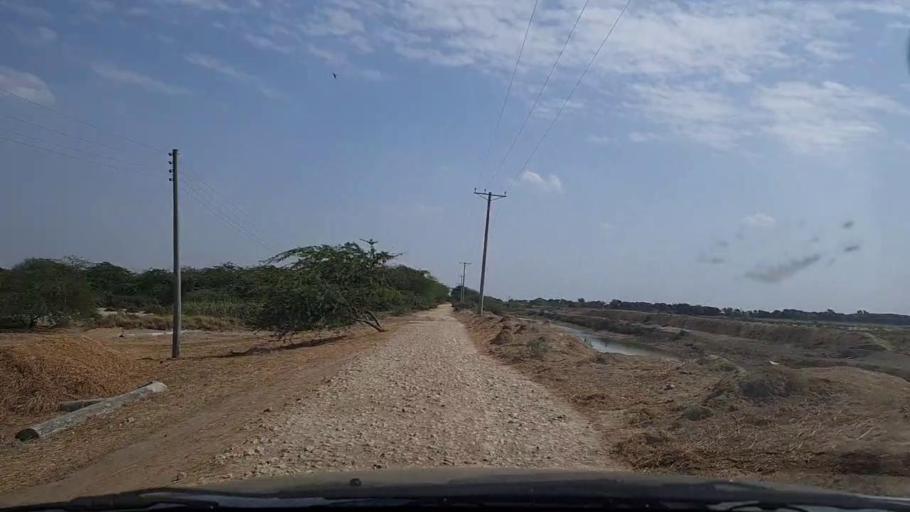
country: PK
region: Sindh
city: Mirpur Batoro
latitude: 24.5670
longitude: 68.1984
